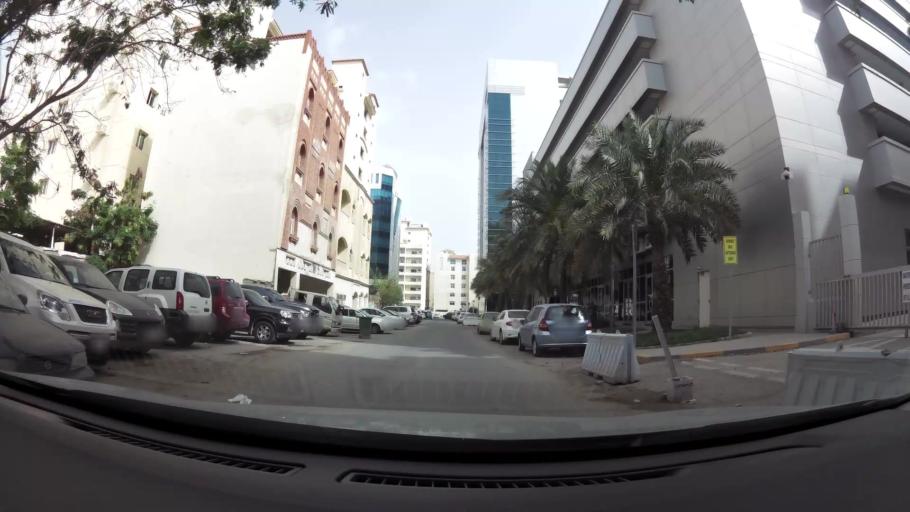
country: QA
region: Baladiyat ad Dawhah
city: Doha
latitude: 25.2736
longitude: 51.5337
